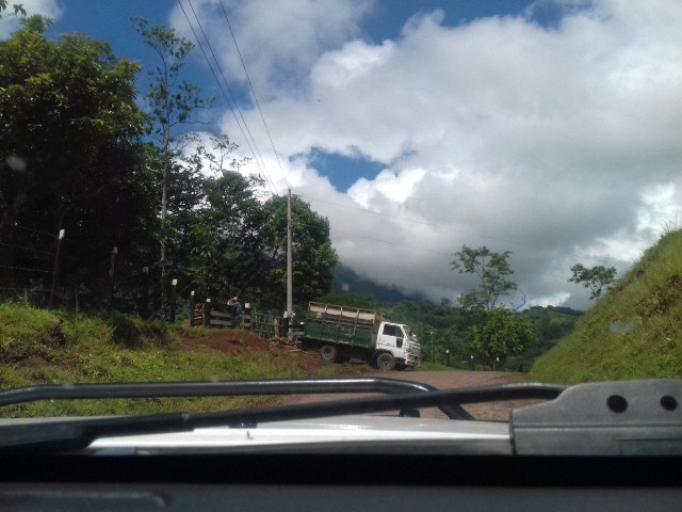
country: NI
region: Matagalpa
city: Rio Blanco
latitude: 12.9819
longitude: -85.1886
